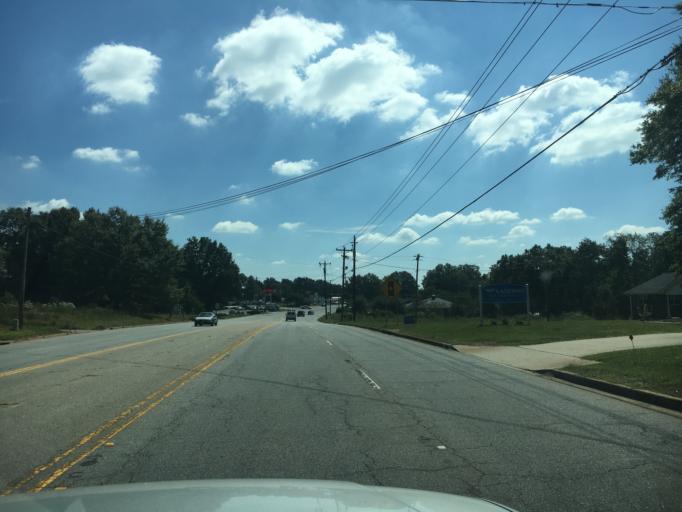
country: US
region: South Carolina
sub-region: Spartanburg County
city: Valley Falls
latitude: 35.0094
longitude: -81.9544
